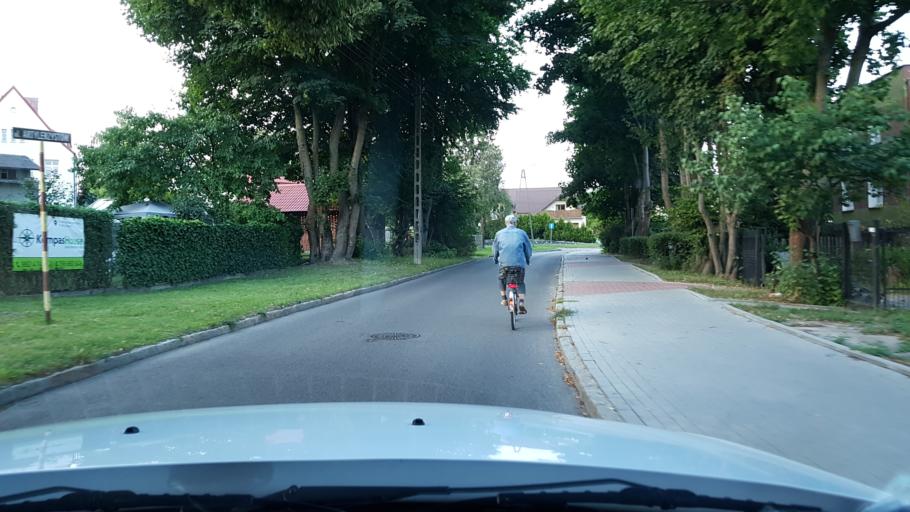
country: PL
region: West Pomeranian Voivodeship
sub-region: Koszalin
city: Koszalin
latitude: 54.1903
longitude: 16.2258
